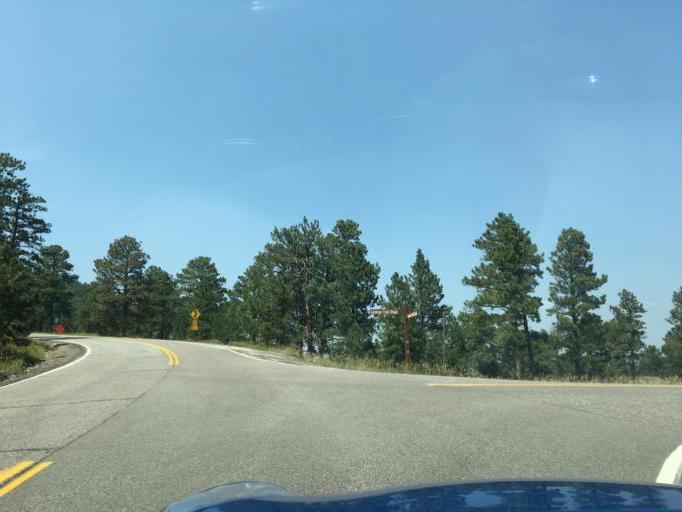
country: US
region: Colorado
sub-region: Jefferson County
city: Genesee
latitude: 39.6962
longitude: -105.2683
